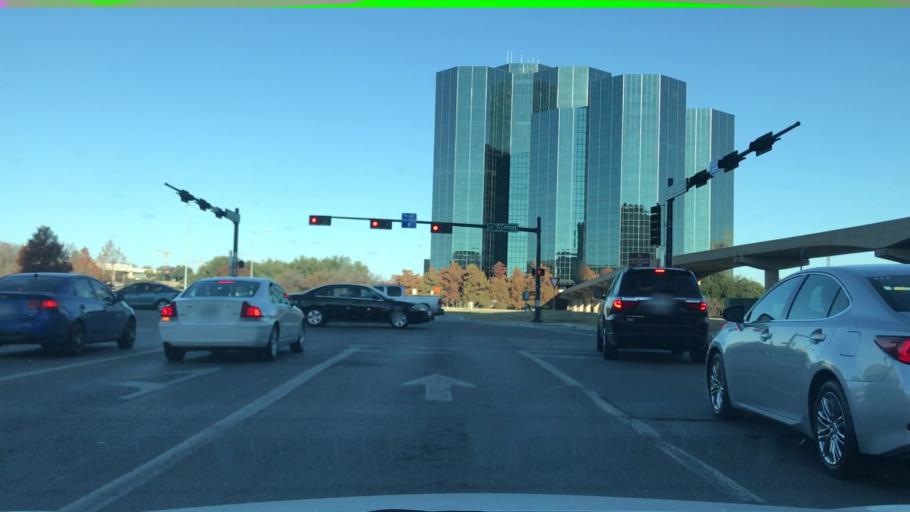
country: US
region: Texas
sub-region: Dallas County
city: Irving
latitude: 32.8687
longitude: -96.9422
